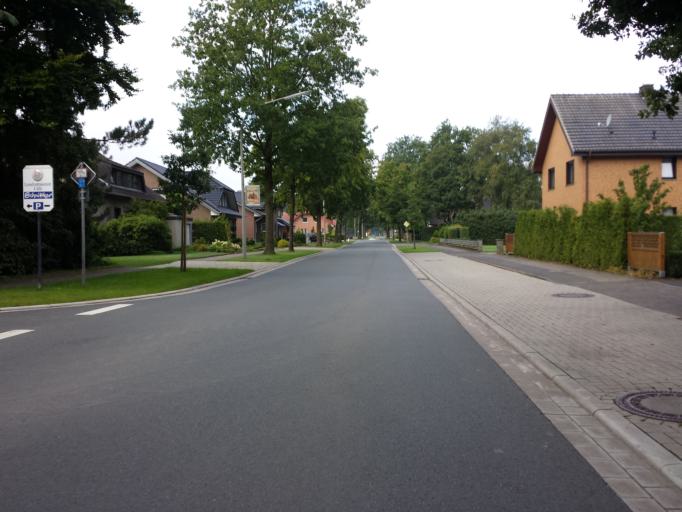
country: DE
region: North Rhine-Westphalia
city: Rietberg
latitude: 51.7867
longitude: 8.4940
